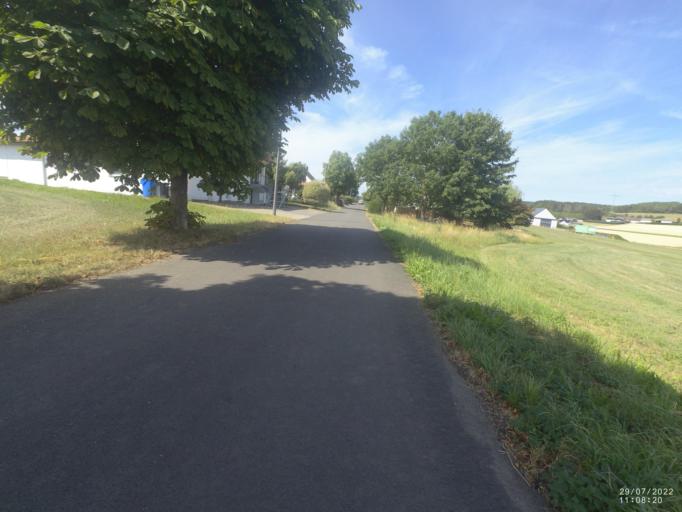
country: DE
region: Rheinland-Pfalz
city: Budesheim
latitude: 50.2208
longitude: 6.5640
